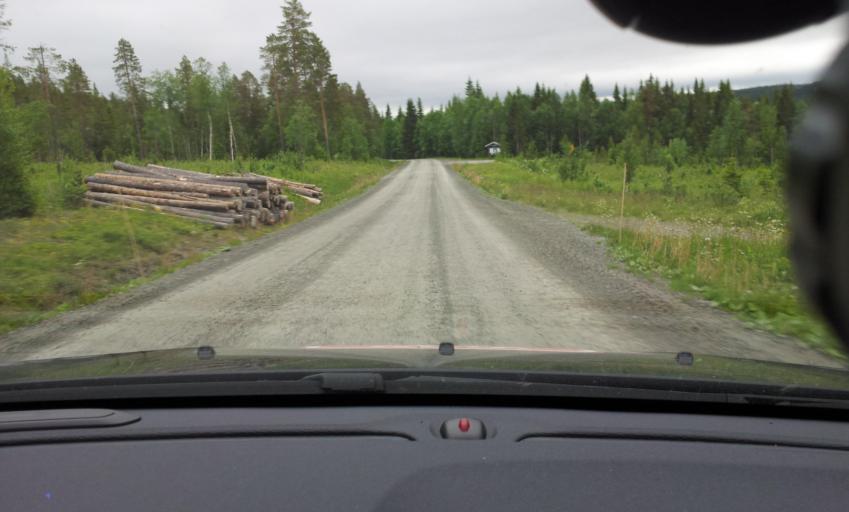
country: SE
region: Jaemtland
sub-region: Are Kommun
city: Jarpen
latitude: 63.2534
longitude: 13.6540
